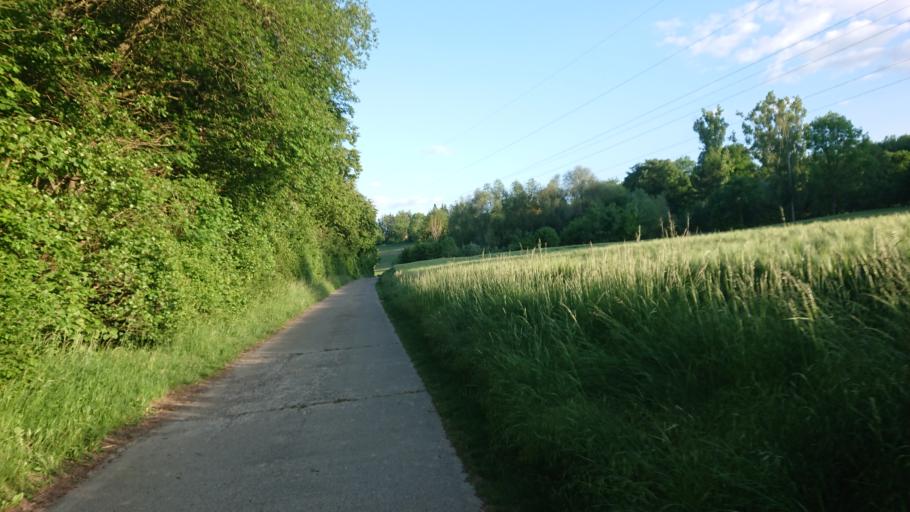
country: DE
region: Lower Saxony
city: Hardegsen
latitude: 51.5958
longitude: 9.8408
